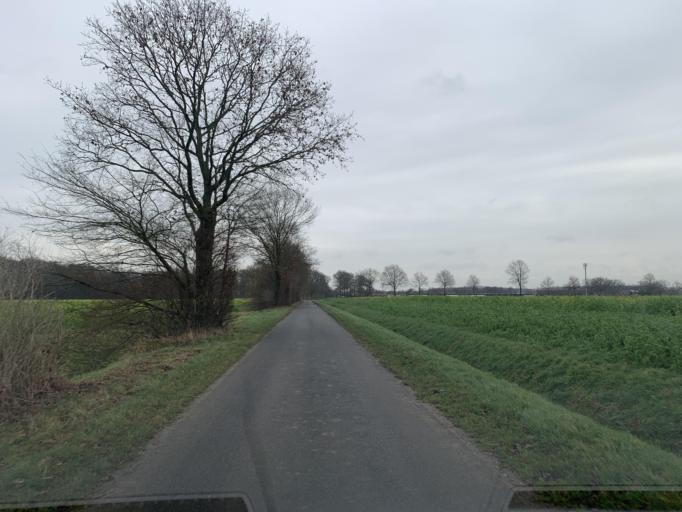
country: DE
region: North Rhine-Westphalia
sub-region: Regierungsbezirk Munster
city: Senden
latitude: 51.8895
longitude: 7.5640
